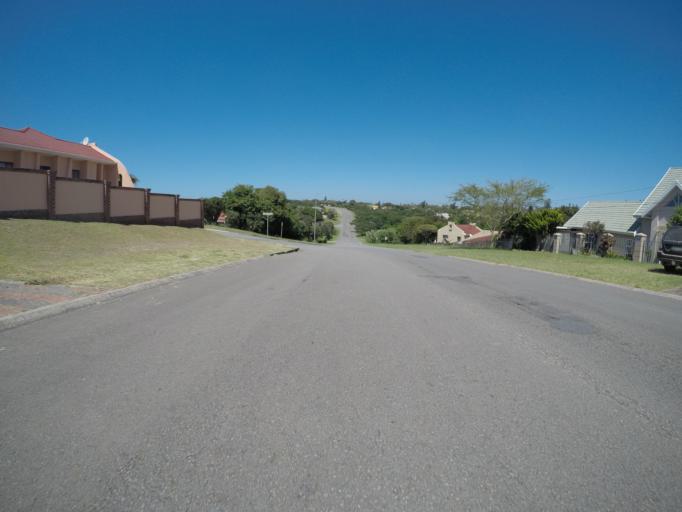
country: ZA
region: Eastern Cape
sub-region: Buffalo City Metropolitan Municipality
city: East London
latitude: -32.9725
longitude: 27.9480
